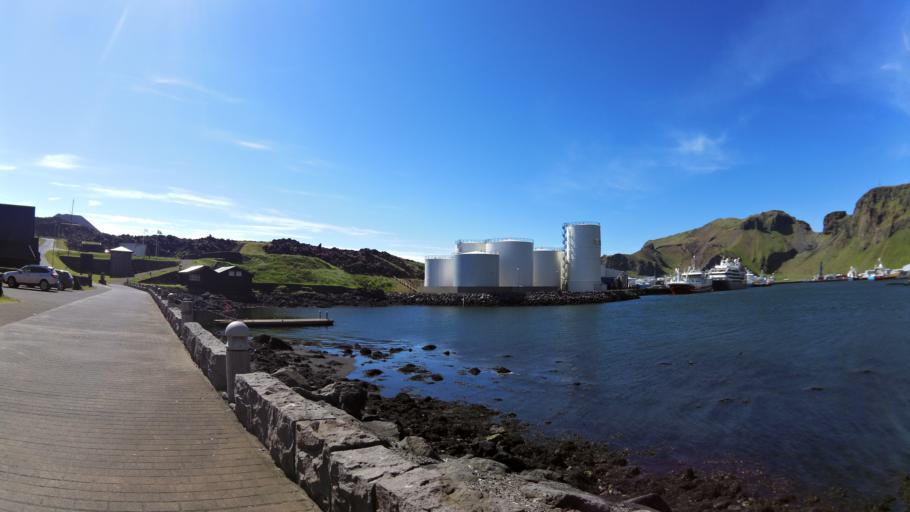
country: IS
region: South
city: Vestmannaeyjar
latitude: 63.4452
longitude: -20.2616
